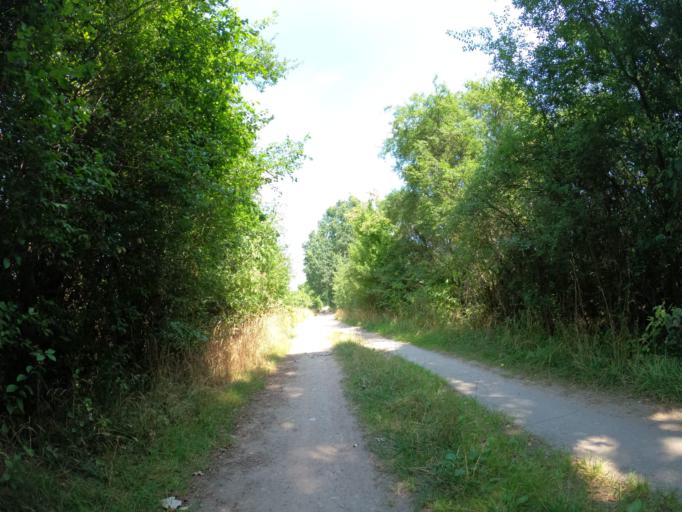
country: DE
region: Brandenburg
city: Mittenwalde
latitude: 53.2918
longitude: 13.5611
